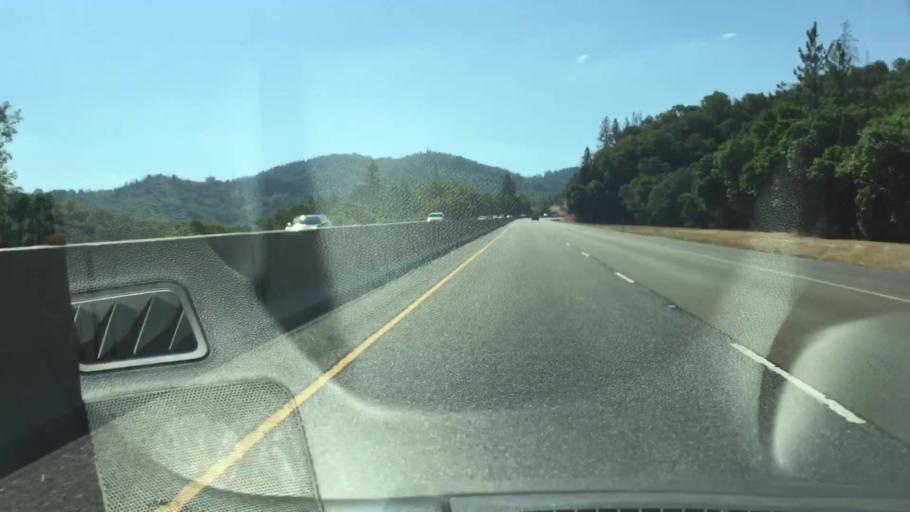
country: US
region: Oregon
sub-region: Douglas County
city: Green
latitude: 43.1208
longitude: -123.3613
